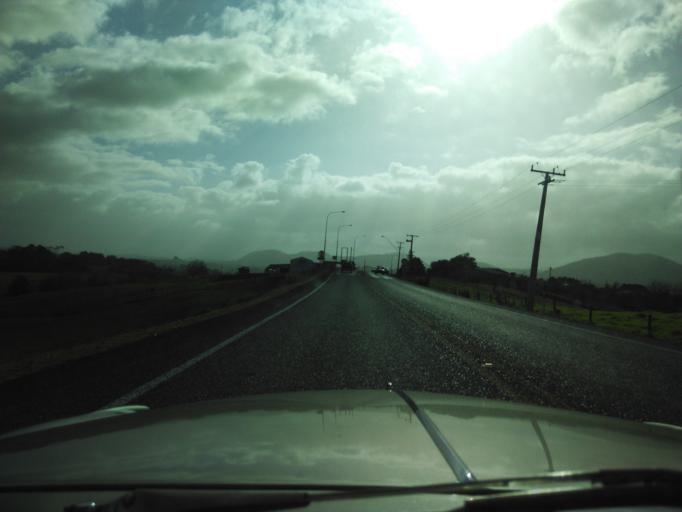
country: NZ
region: Auckland
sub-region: Auckland
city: Wellsford
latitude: -36.1737
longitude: 174.4488
